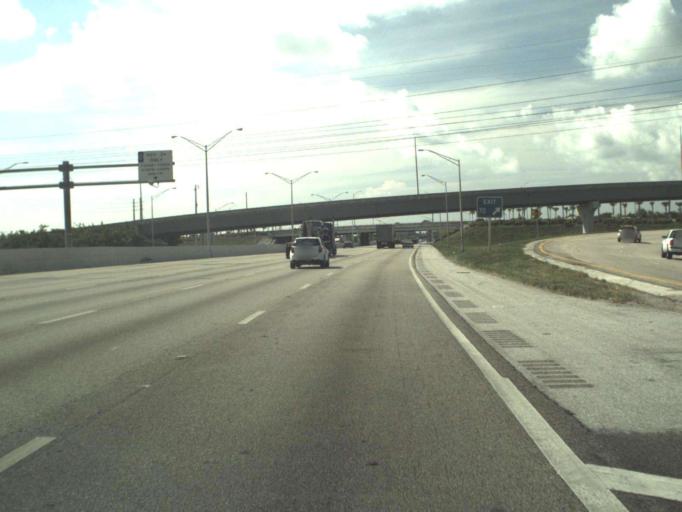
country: US
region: Florida
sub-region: Palm Beach County
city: West Palm Beach
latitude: 26.7090
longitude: -80.0782
